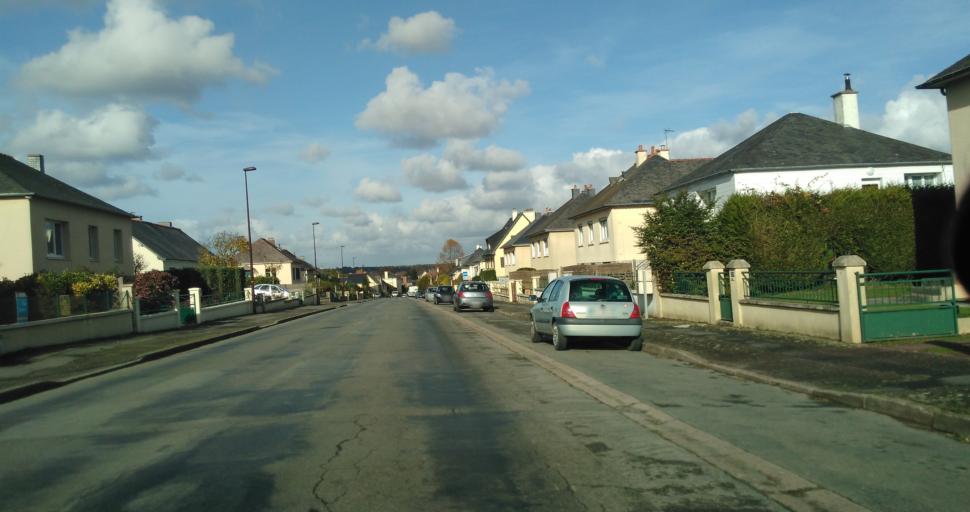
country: FR
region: Brittany
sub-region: Departement d'Ille-et-Vilaine
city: Montauban-de-Bretagne
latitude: 48.1859
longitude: -2.0504
